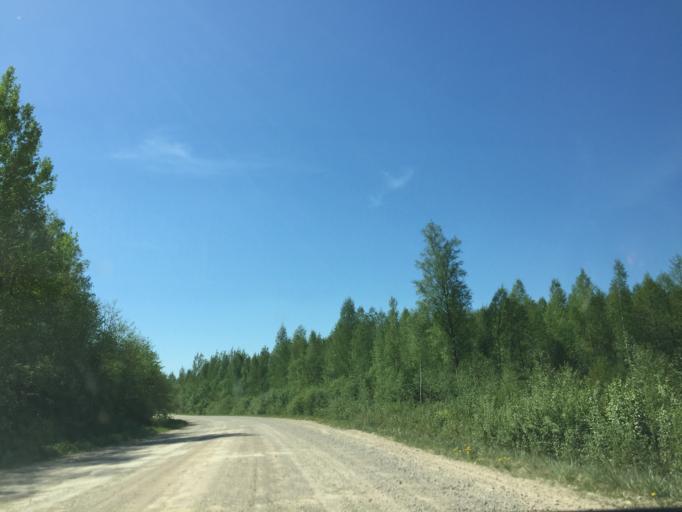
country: LV
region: Kegums
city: Kegums
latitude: 56.8783
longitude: 24.7805
